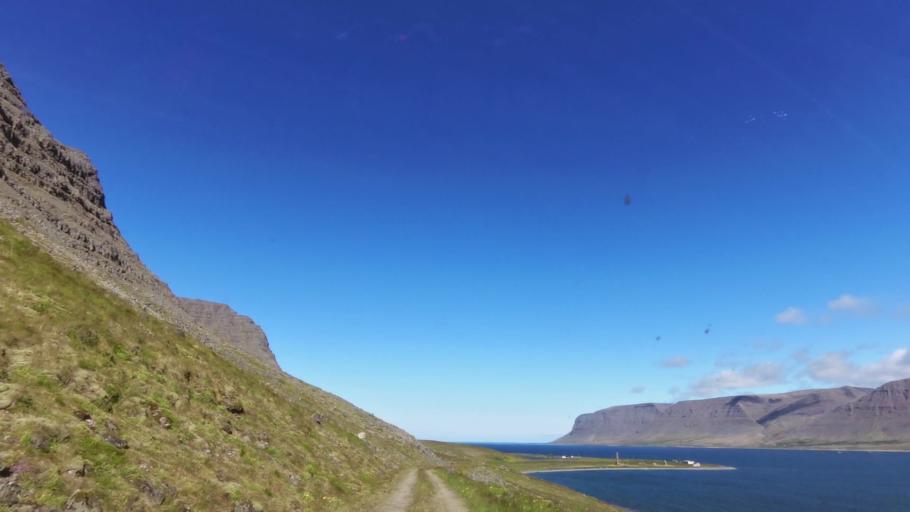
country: IS
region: West
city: Olafsvik
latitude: 65.6337
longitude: -23.9225
